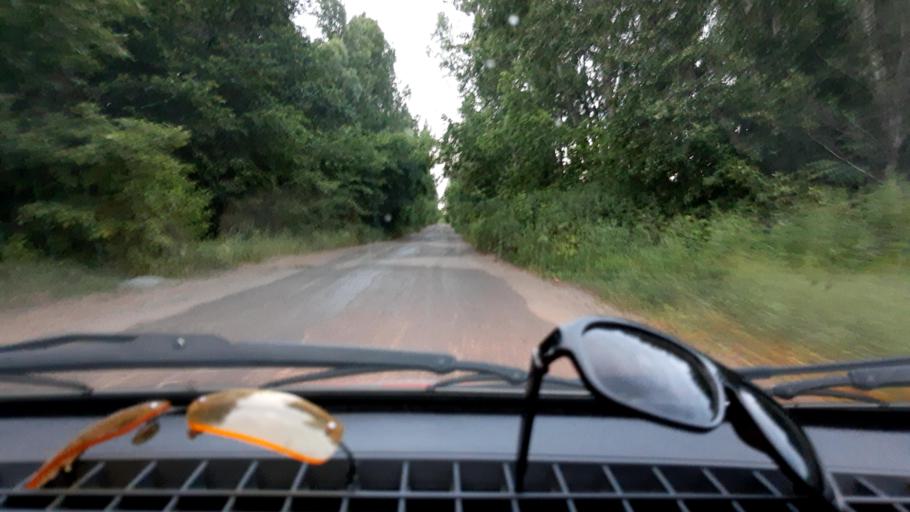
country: RU
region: Bashkortostan
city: Avdon
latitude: 54.6631
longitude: 55.8222
